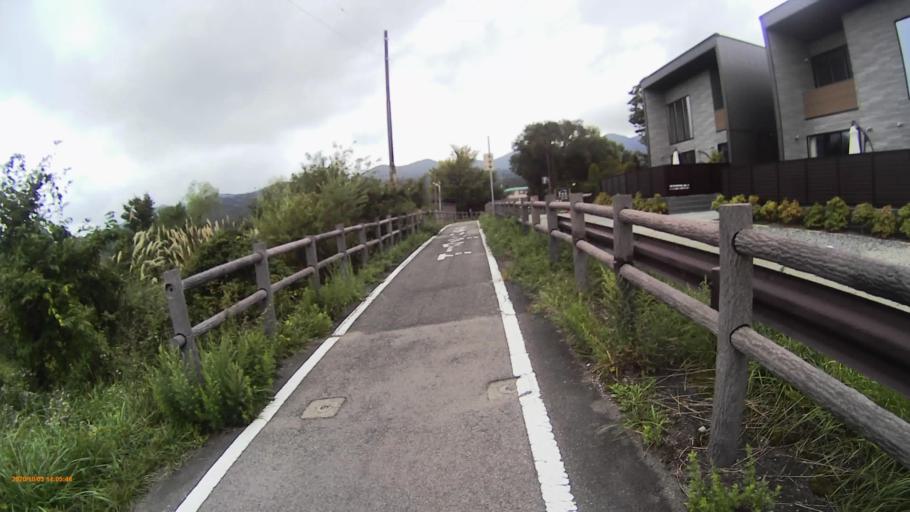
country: JP
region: Shizuoka
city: Gotemba
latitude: 35.4238
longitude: 138.9018
